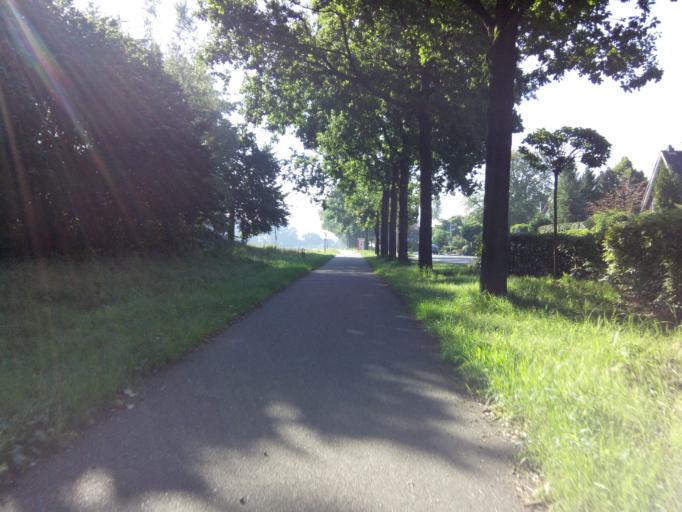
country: NL
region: Utrecht
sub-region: Gemeente Utrechtse Heuvelrug
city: Amerongen
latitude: 51.9913
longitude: 5.4804
